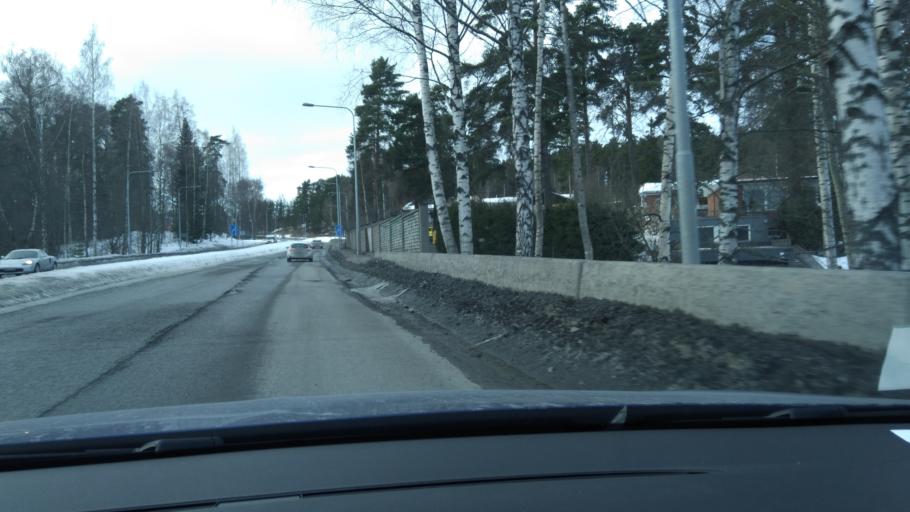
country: FI
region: Pirkanmaa
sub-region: Tampere
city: Pirkkala
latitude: 61.4993
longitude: 23.6514
